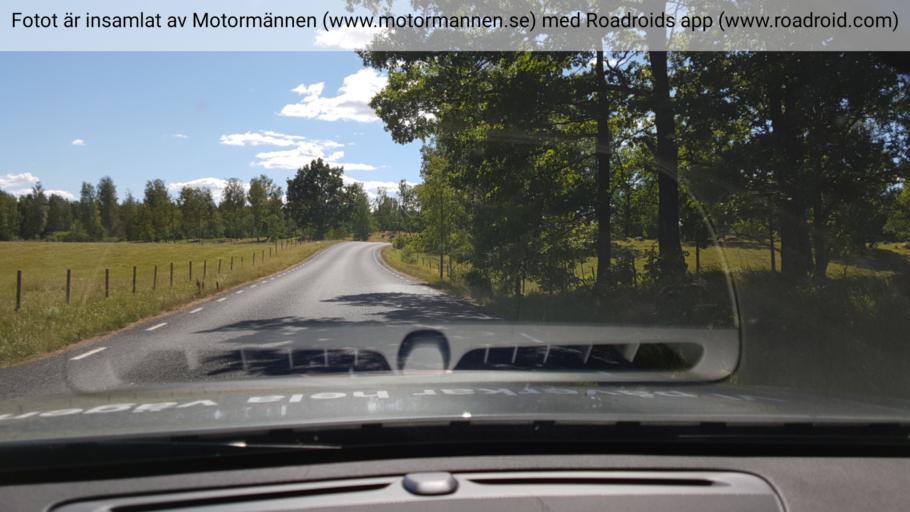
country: SE
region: Soedermanland
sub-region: Flens Kommun
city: Halleforsnas
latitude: 59.1641
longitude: 16.5214
